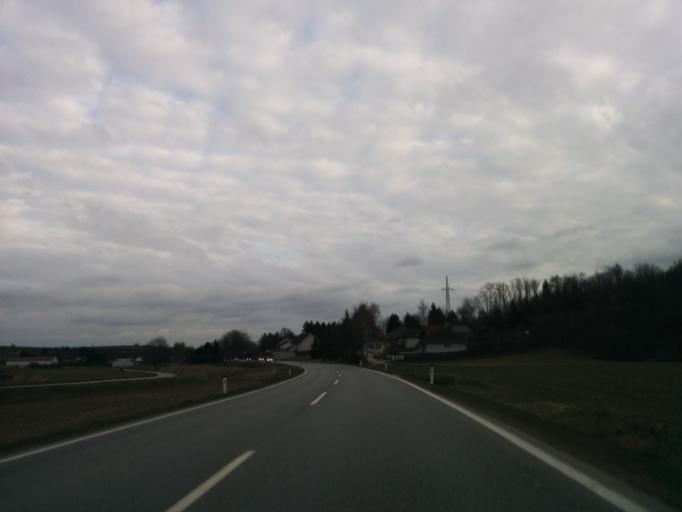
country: AT
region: Lower Austria
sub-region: Politischer Bezirk Mistelbach
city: Asparn an der Zaya
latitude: 48.6143
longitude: 16.5267
